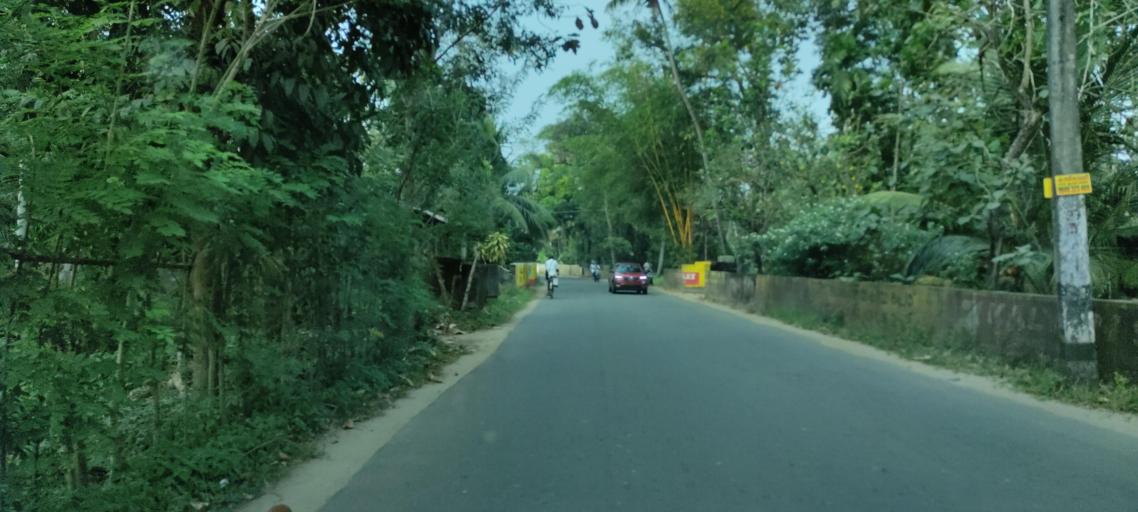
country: IN
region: Kerala
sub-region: Kottayam
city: Vaikam
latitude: 9.7209
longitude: 76.4162
